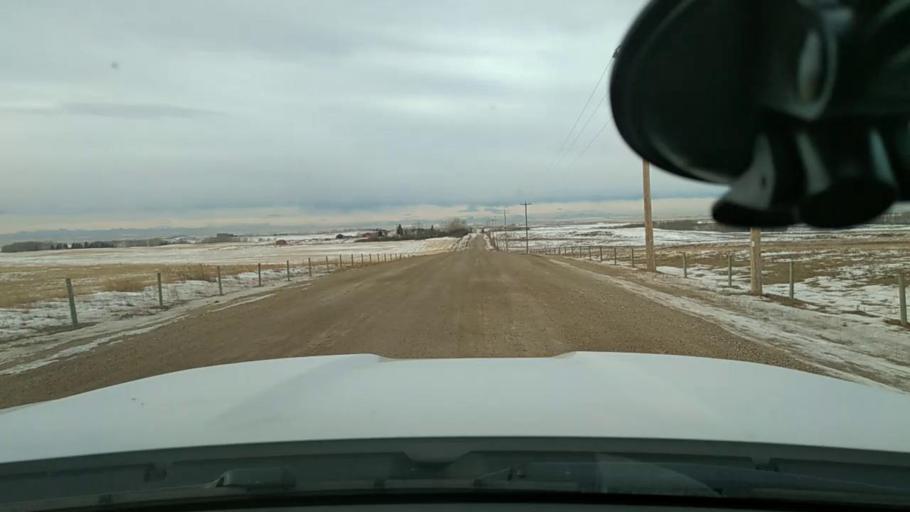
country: CA
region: Alberta
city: Airdrie
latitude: 51.2417
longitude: -113.9123
